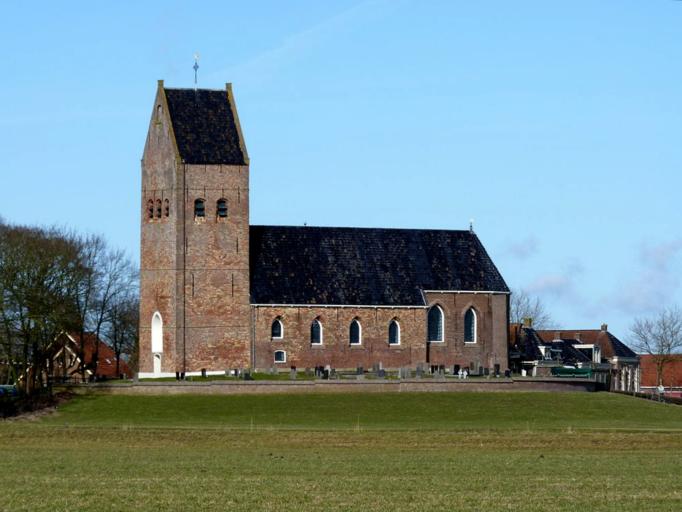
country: NL
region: Friesland
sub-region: Gemeente Ferwerderadiel
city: Burdaard
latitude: 53.3010
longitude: 5.8496
